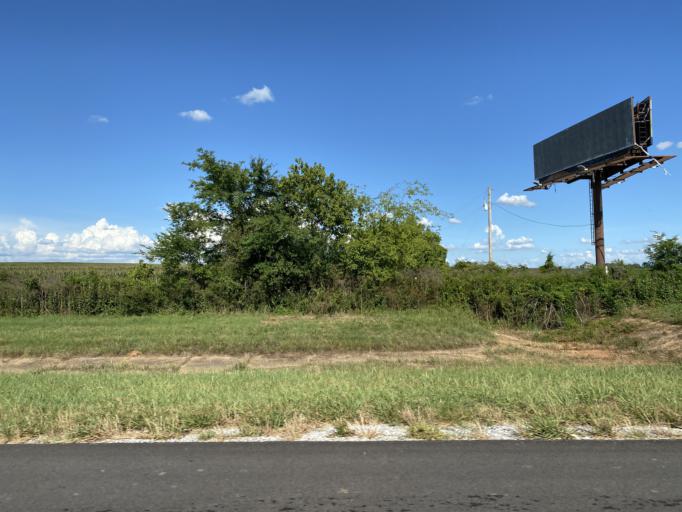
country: US
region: Alabama
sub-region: Limestone County
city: Athens
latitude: 34.7453
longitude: -86.9384
